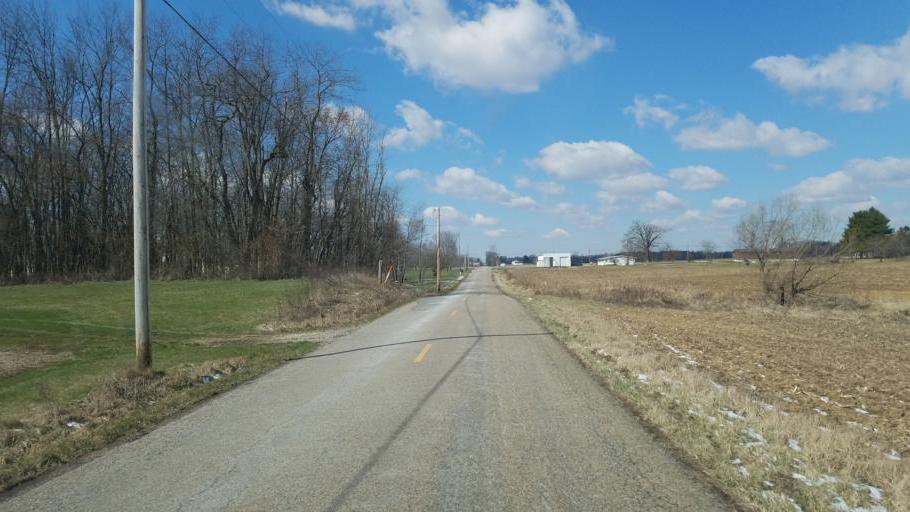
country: US
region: Ohio
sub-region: Licking County
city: Utica
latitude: 40.2664
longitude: -82.5132
